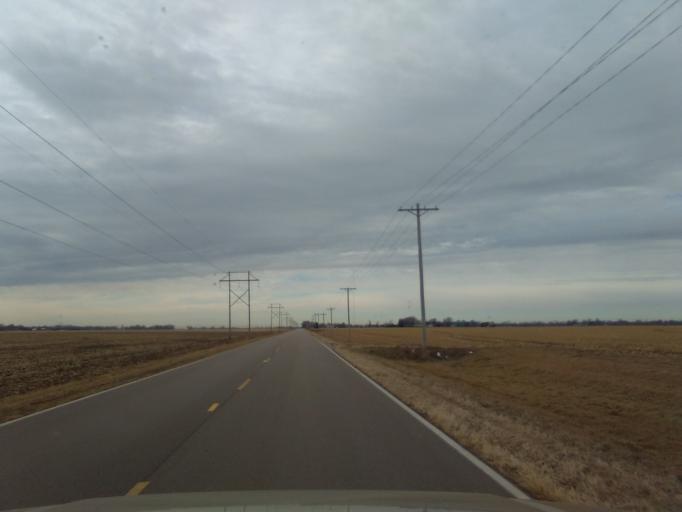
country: US
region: Nebraska
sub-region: Buffalo County
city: Gibbon
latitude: 40.6550
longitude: -98.8238
